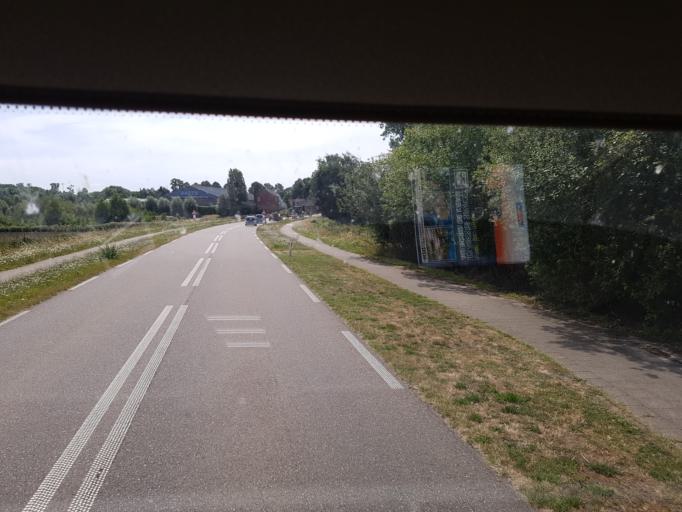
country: NL
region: Limburg
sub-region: Gemeente Leudal
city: Kelpen-Oler
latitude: 51.2428
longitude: 5.8194
